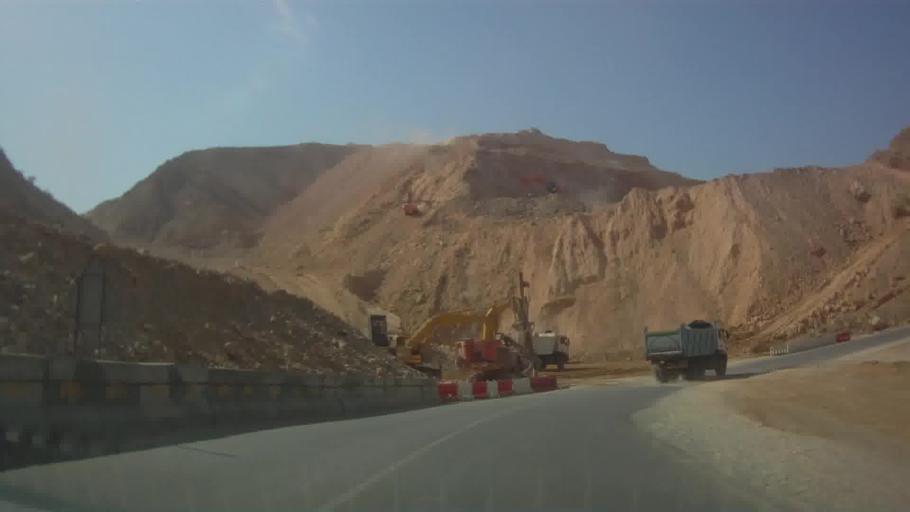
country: OM
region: Muhafazat Masqat
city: Muscat
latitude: 23.5103
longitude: 58.7234
